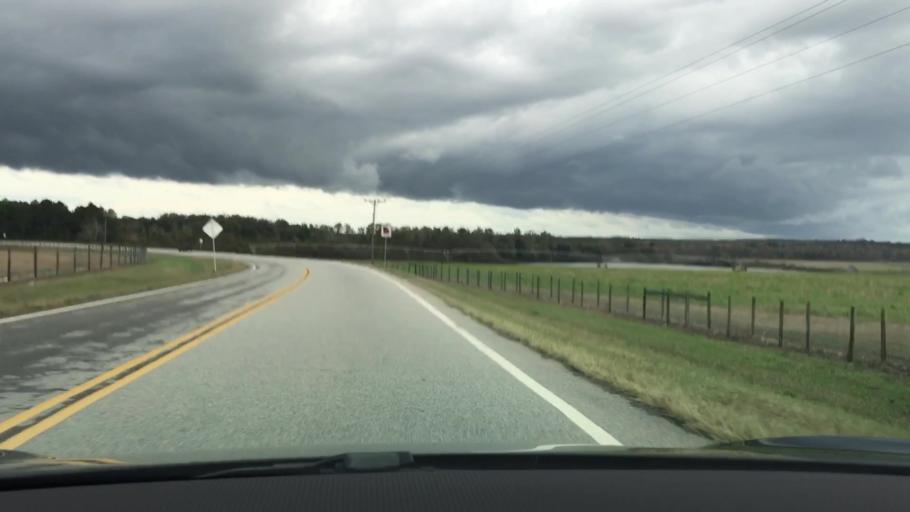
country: US
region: Georgia
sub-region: Oconee County
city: Watkinsville
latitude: 33.7257
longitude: -83.3022
